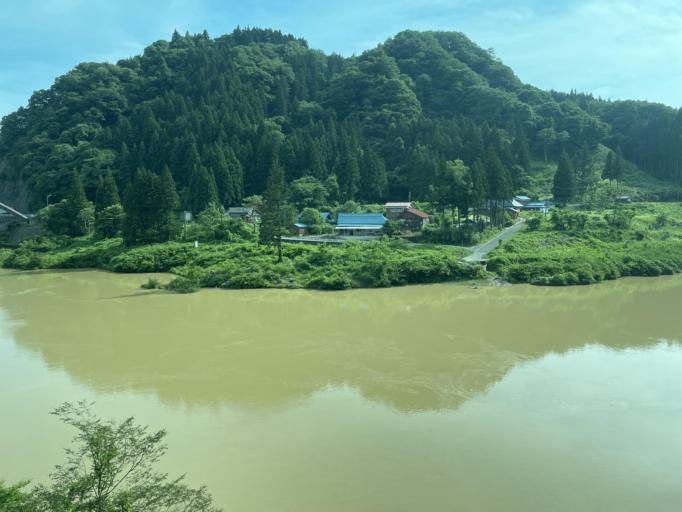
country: JP
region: Fukushima
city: Kitakata
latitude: 37.6711
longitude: 139.5911
